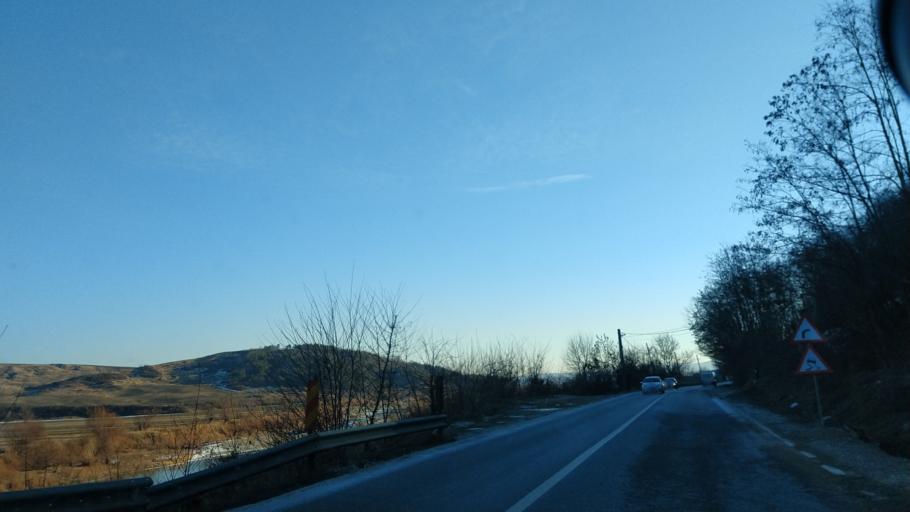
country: RO
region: Bacau
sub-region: Comuna Helegiu
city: Bratila
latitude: 46.3047
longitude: 26.7523
